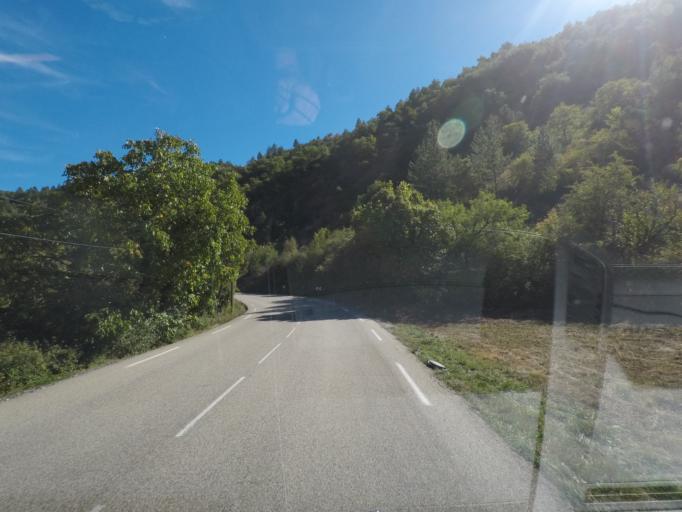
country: FR
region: Rhone-Alpes
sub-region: Departement de la Drome
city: Buis-les-Baronnies
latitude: 44.4218
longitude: 5.3212
